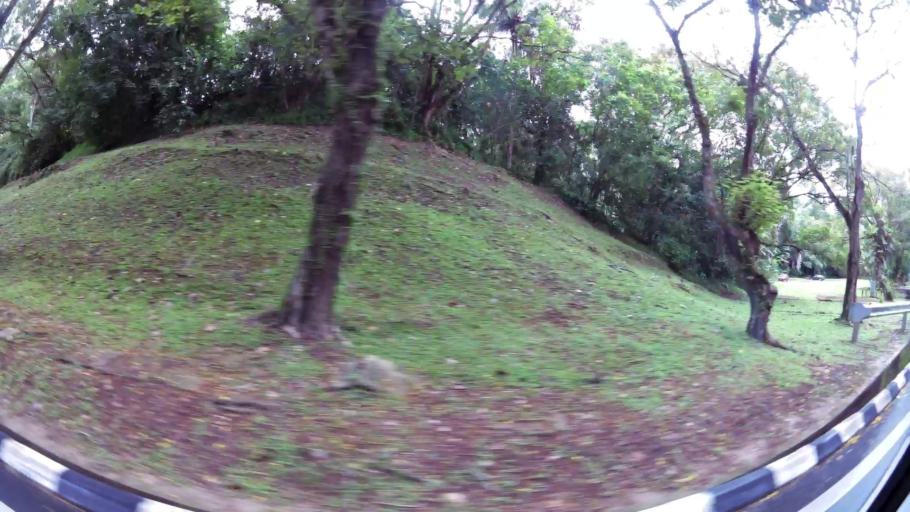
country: BN
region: Brunei and Muara
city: Bandar Seri Begawan
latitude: 4.9024
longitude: 114.9323
